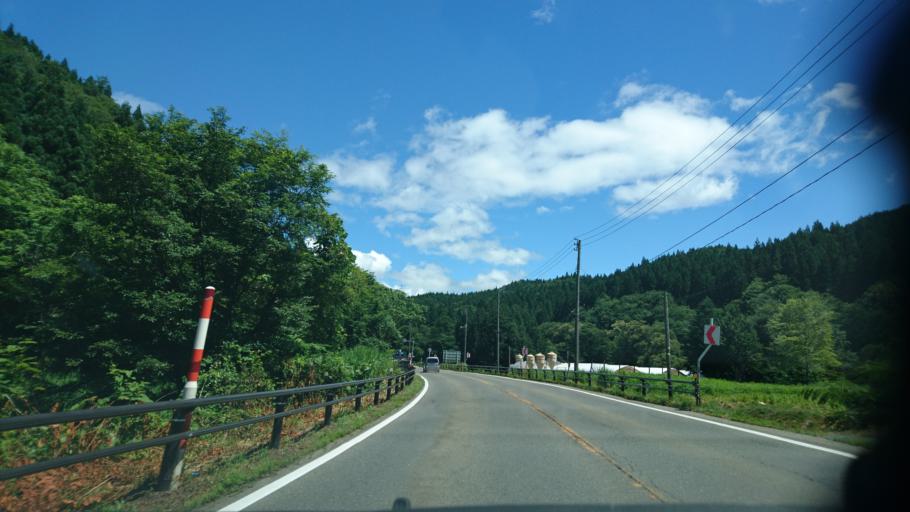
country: JP
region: Akita
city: Kakunodatemachi
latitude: 39.6533
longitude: 140.6716
